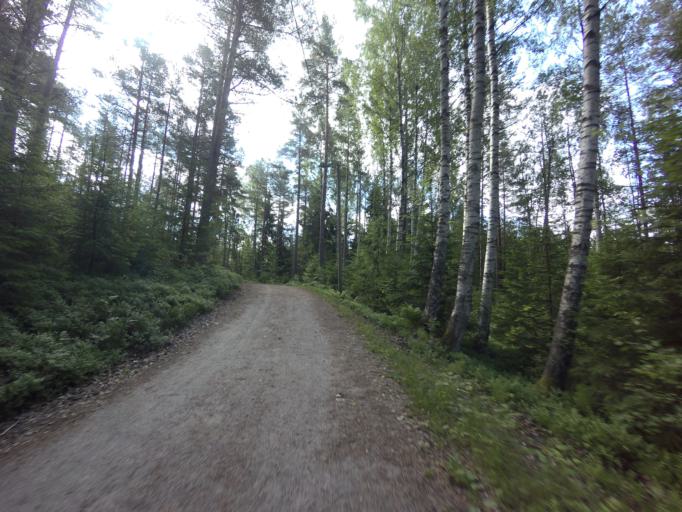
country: FI
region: Uusimaa
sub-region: Helsinki
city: Espoo
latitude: 60.1805
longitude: 24.6327
